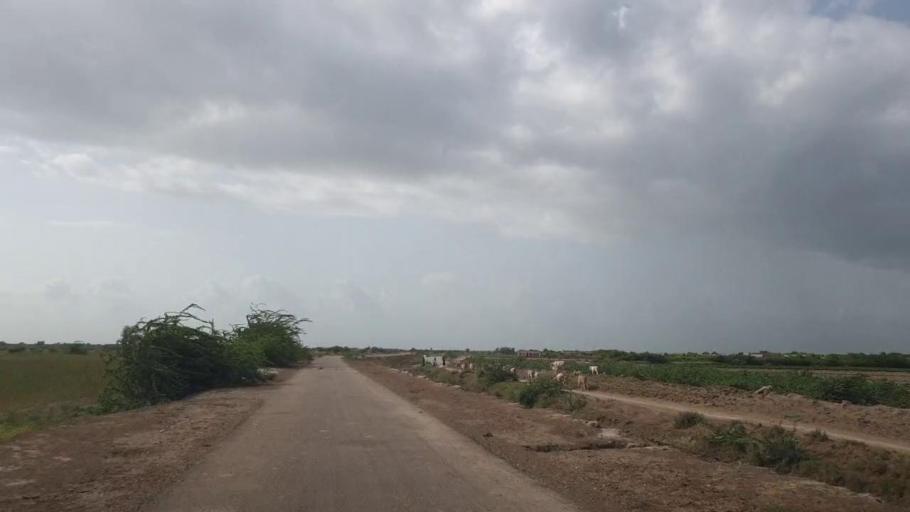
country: PK
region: Sindh
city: Kadhan
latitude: 24.5665
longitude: 69.0632
